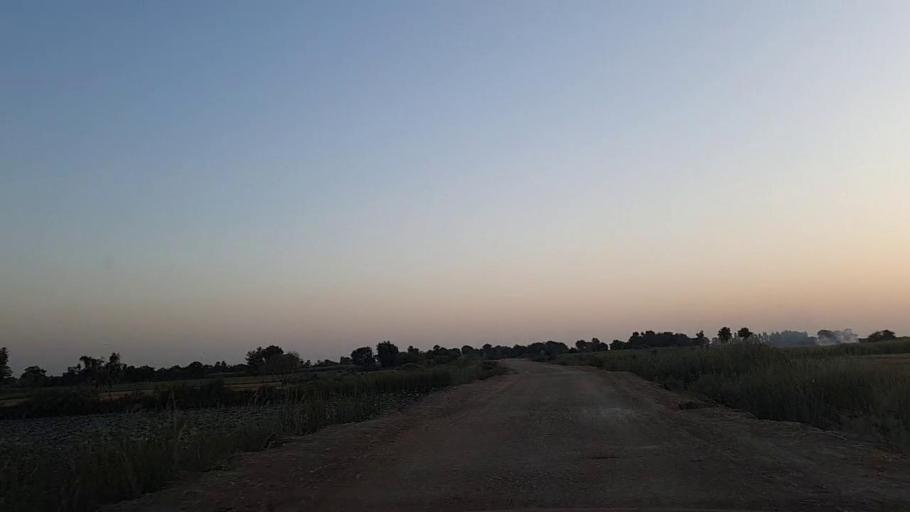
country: PK
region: Sindh
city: Mirpur Batoro
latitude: 24.6213
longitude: 68.1842
